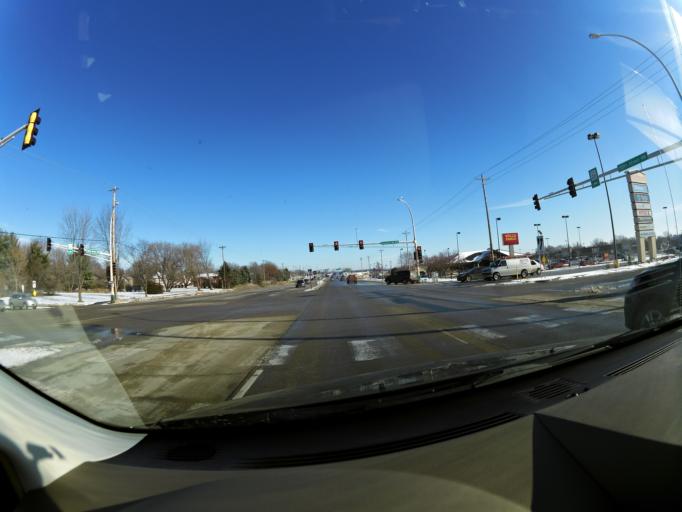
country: US
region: Minnesota
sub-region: Olmsted County
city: Rochester
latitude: 44.0796
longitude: -92.5149
